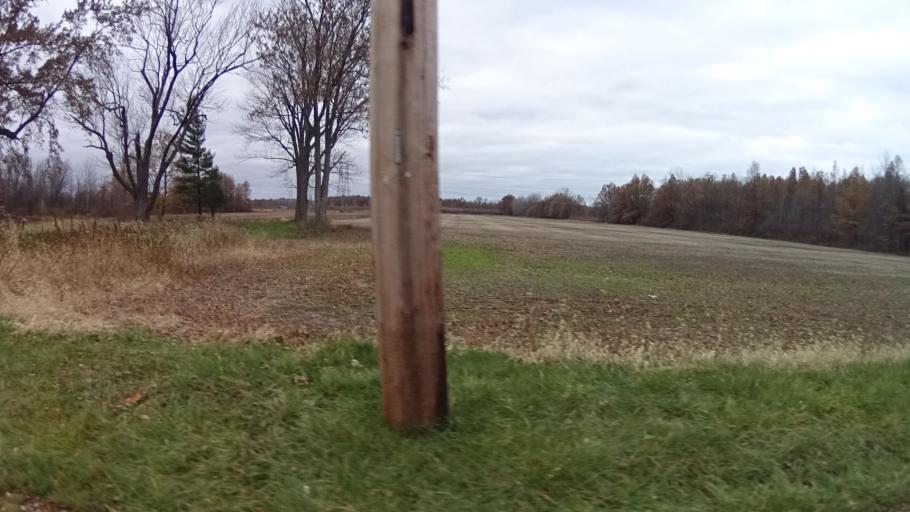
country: US
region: Ohio
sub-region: Lorain County
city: Avon Lake
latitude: 41.4817
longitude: -82.0471
